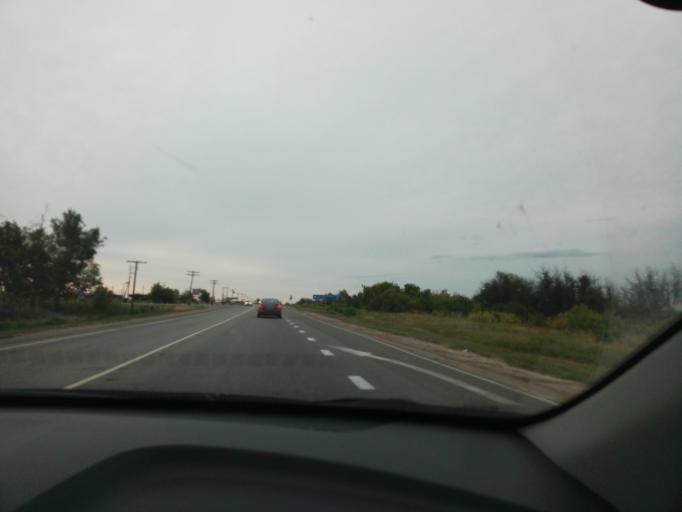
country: RU
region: Volgograd
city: Dubovka
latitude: 49.1090
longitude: 44.8099
